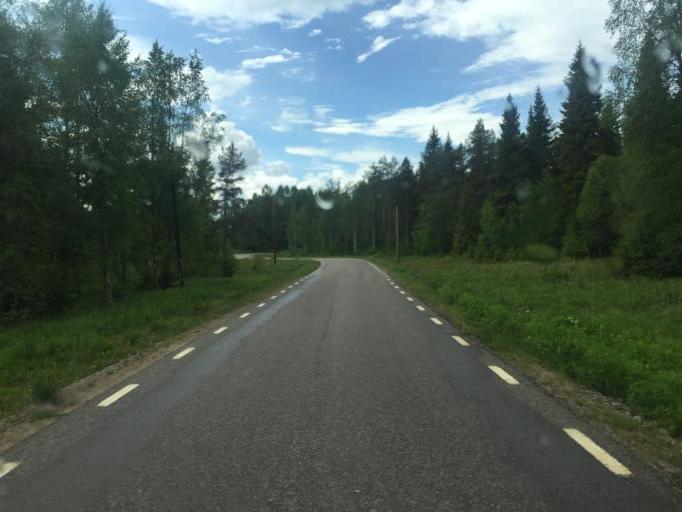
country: SE
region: Vaermland
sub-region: Hagfors Kommun
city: Hagfors
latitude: 60.2907
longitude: 13.8649
